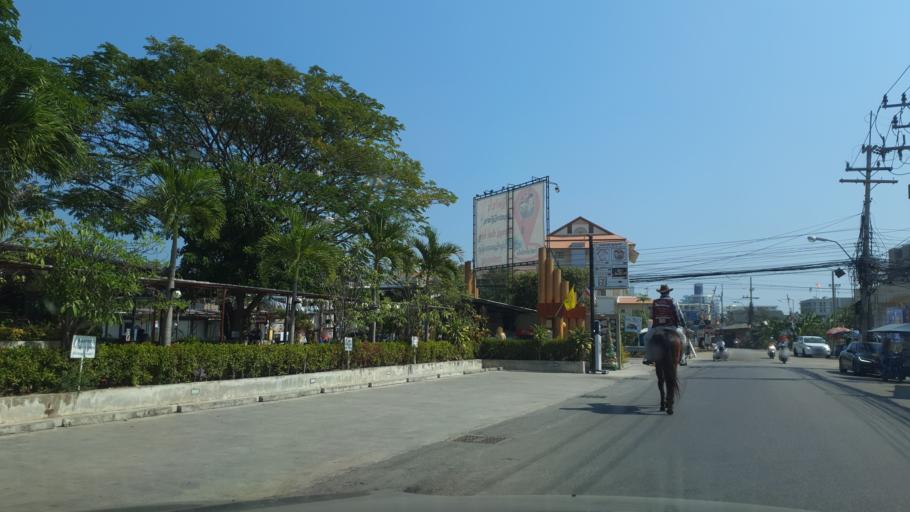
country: TH
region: Prachuap Khiri Khan
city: Hua Hin
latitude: 12.5544
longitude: 99.9572
